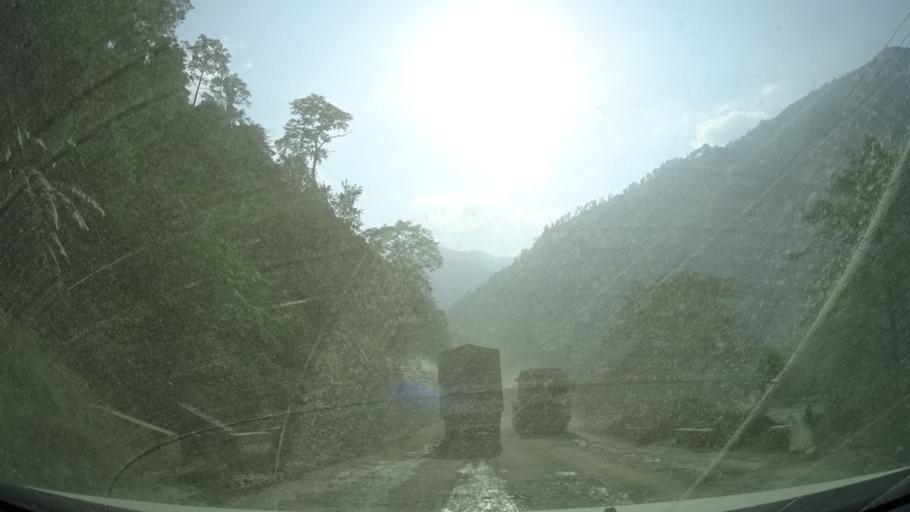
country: NP
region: Central Region
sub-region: Narayani Zone
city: Bharatpur
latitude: 27.8139
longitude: 84.4368
